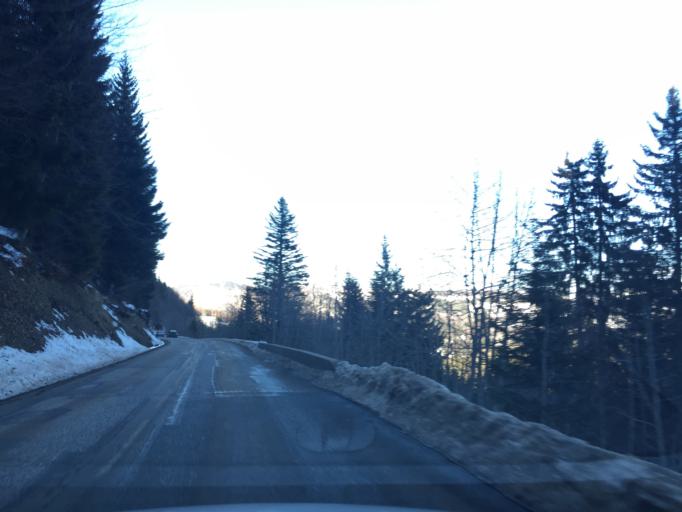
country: FR
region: Rhone-Alpes
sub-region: Departement de la Savoie
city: Mouxy
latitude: 45.6839
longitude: 5.9963
